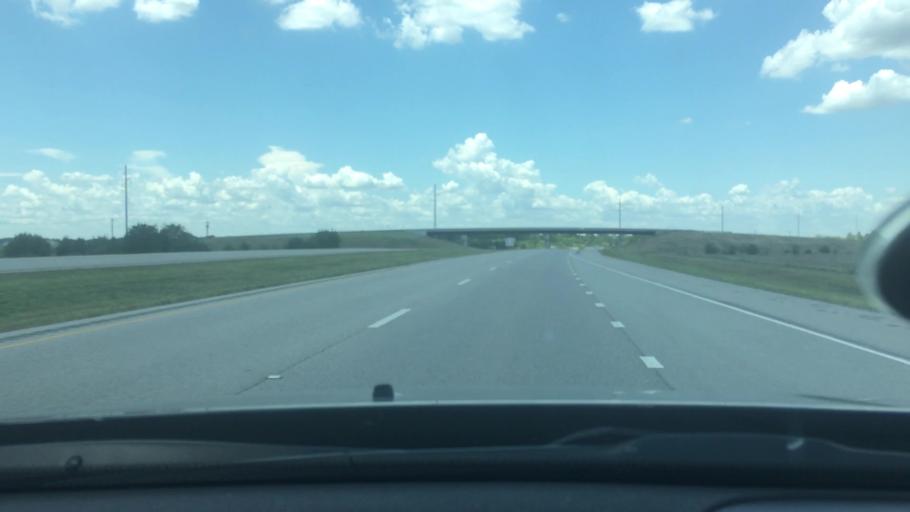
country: US
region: Oklahoma
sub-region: Bryan County
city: Calera
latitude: 33.9741
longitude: -96.4225
